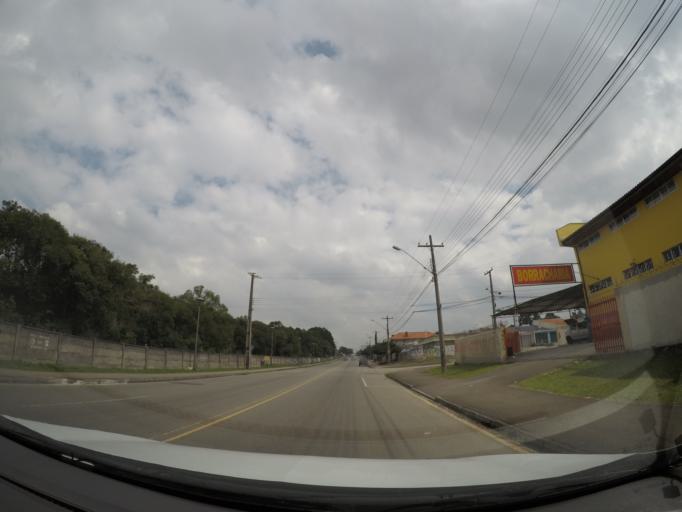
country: BR
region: Parana
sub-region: Sao Jose Dos Pinhais
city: Sao Jose dos Pinhais
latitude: -25.5062
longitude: -49.2445
